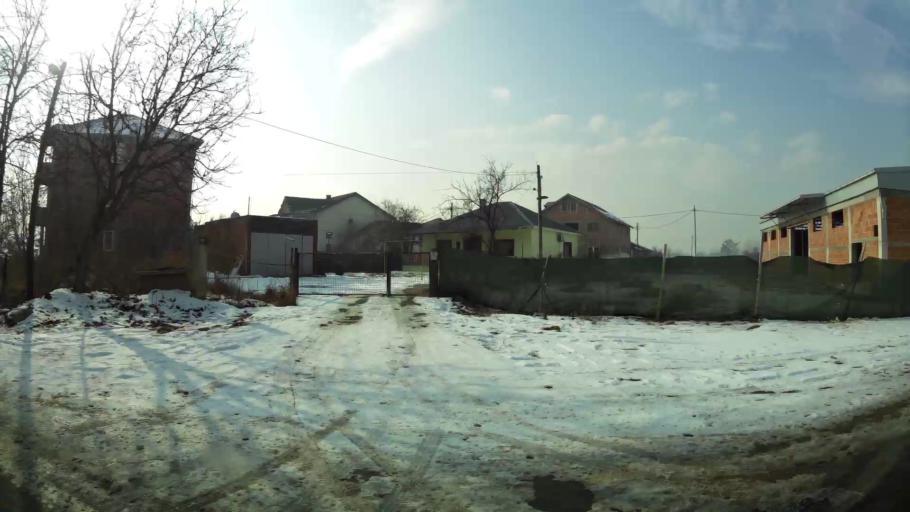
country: MK
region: Kisela Voda
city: Kisela Voda
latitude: 41.9868
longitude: 21.5002
